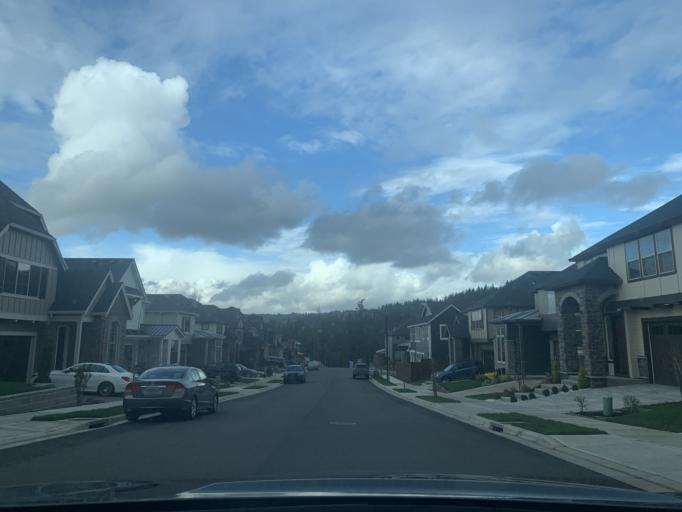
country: US
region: Oregon
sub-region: Washington County
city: Cedar Mill
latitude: 45.5504
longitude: -122.8050
